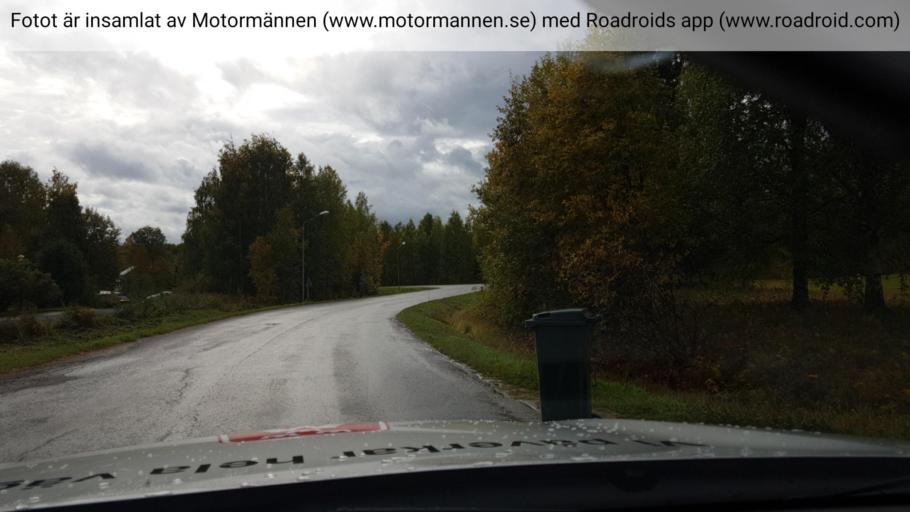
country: SE
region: Norrbotten
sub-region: Alvsbyns Kommun
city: AElvsbyn
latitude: 66.0893
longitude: 20.8943
